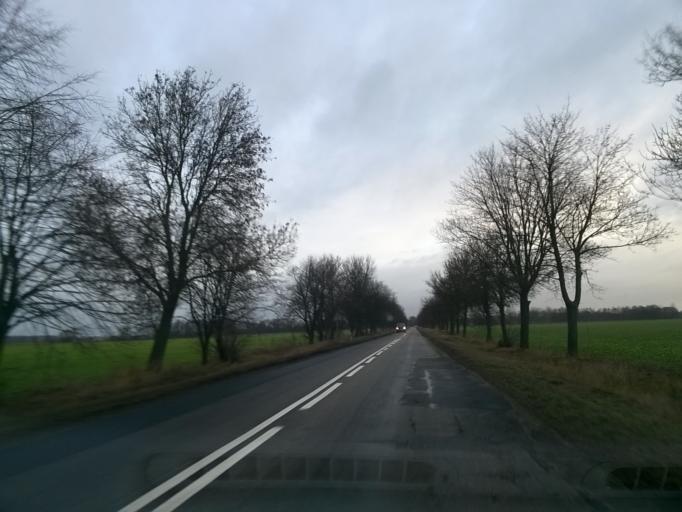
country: PL
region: Greater Poland Voivodeship
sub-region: Powiat wagrowiecki
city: Wagrowiec
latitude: 52.8458
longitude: 17.2574
